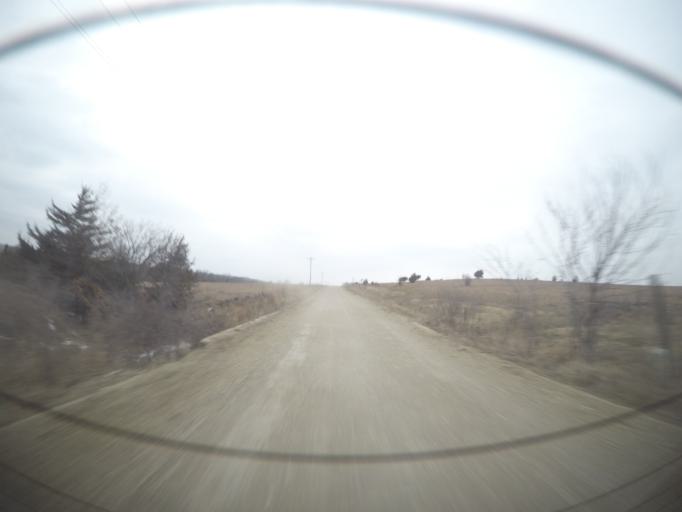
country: US
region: Kansas
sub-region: Pottawatomie County
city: Wamego
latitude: 39.1517
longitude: -96.2719
